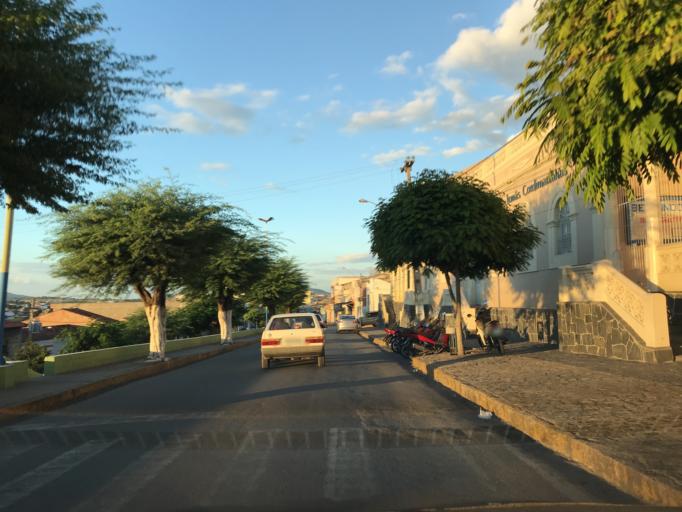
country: BR
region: Pernambuco
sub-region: Bezerros
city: Bezerros
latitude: -8.2367
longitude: -35.7570
